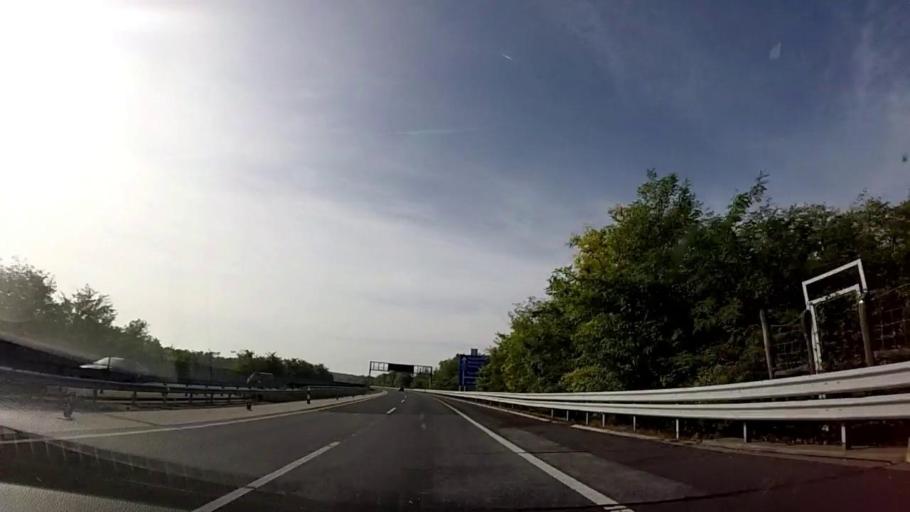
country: HU
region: Somogy
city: Balatonfoldvar
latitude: 46.8275
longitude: 17.9333
